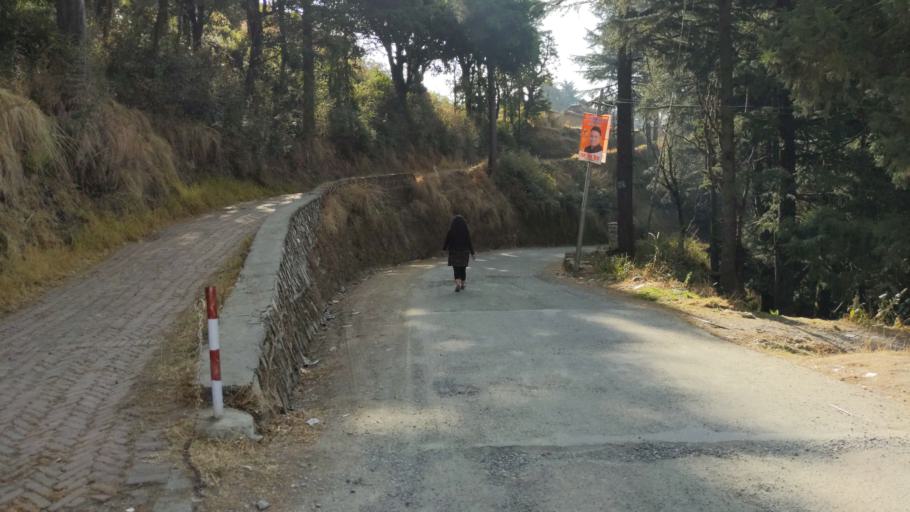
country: IN
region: Uttarakhand
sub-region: Almora
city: Almora
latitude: 29.4722
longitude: 79.6483
